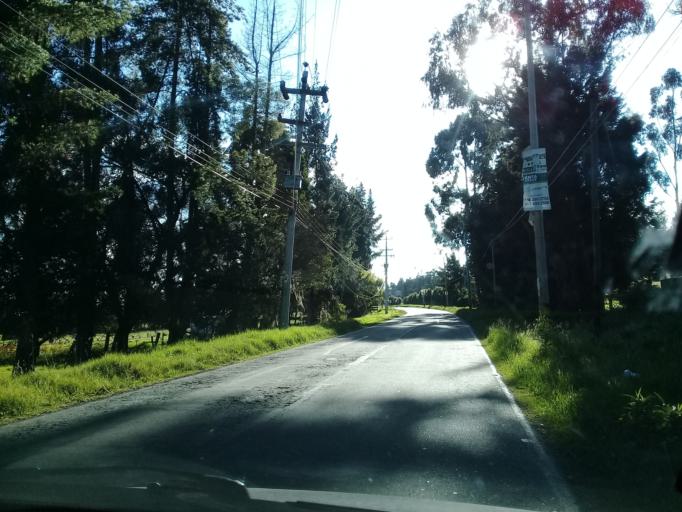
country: CO
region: Cundinamarca
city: Tenjo
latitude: 4.8876
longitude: -74.1181
